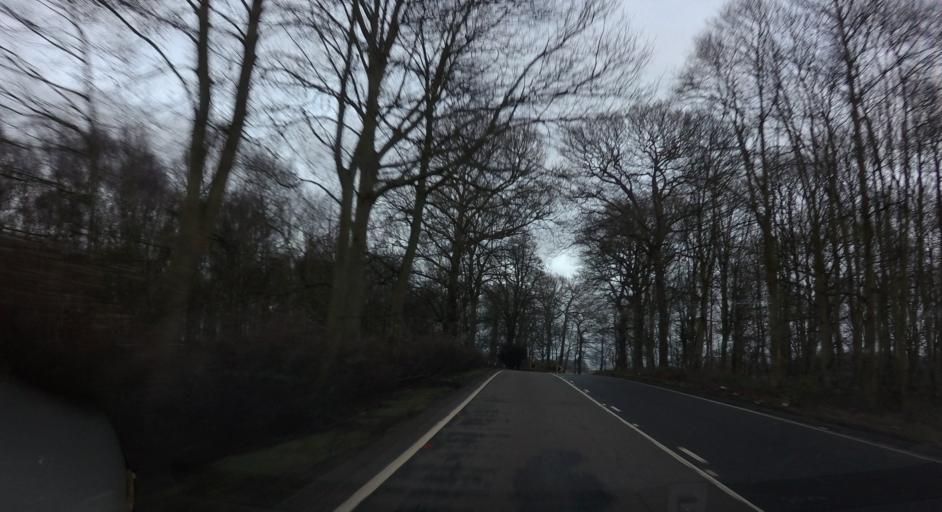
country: GB
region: Scotland
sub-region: Fife
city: Limekilns
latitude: 56.0455
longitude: -3.4766
